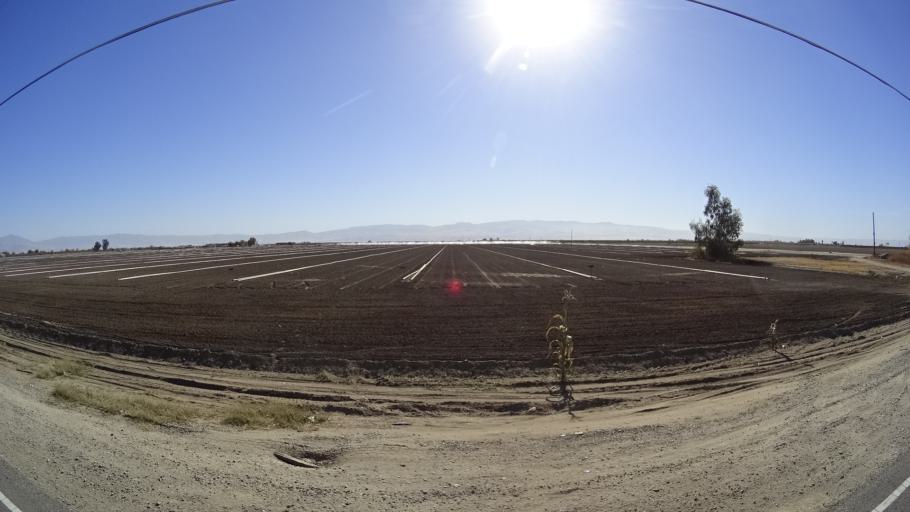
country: US
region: California
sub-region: Kern County
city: Greenfield
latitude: 35.2670
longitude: -119.0555
